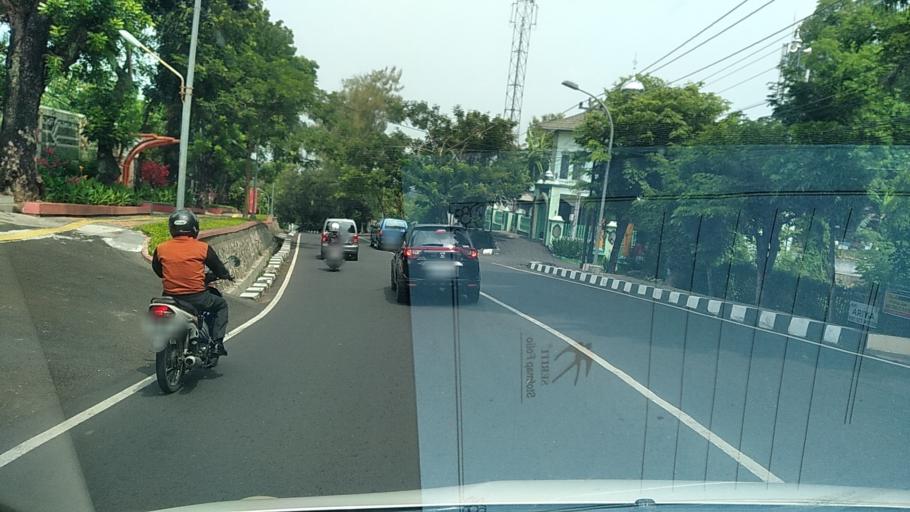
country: ID
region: Central Java
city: Semarang
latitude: -7.0000
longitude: 110.4204
